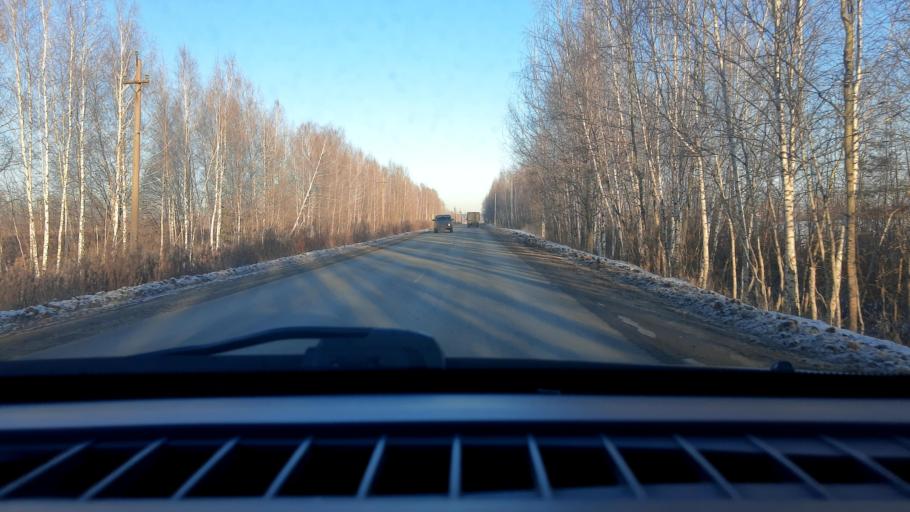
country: RU
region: Nizjnij Novgorod
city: Bor
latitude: 56.3861
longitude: 44.0794
